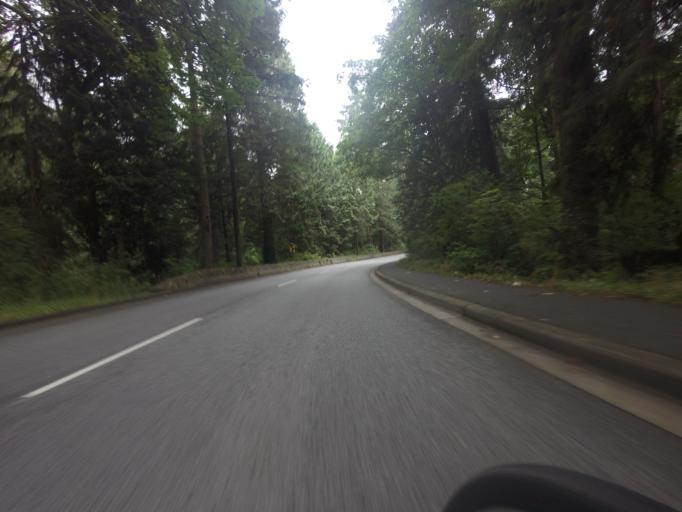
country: CA
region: British Columbia
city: West End
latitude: 49.3019
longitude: -123.1540
